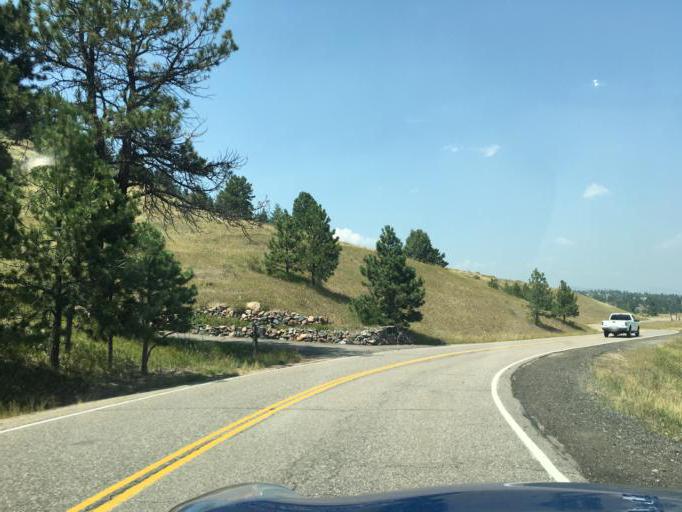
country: US
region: Colorado
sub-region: Jefferson County
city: Genesee
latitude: 39.7002
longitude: -105.2728
